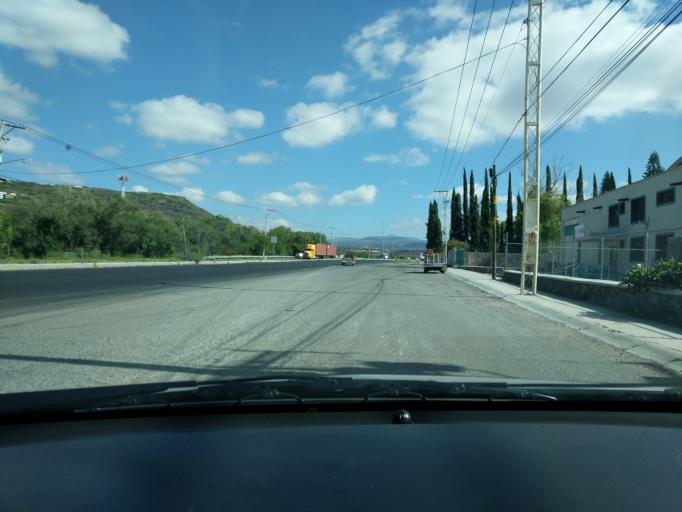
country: MX
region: Queretaro
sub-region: Queretaro
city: Patria Nueva
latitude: 20.6301
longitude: -100.4985
